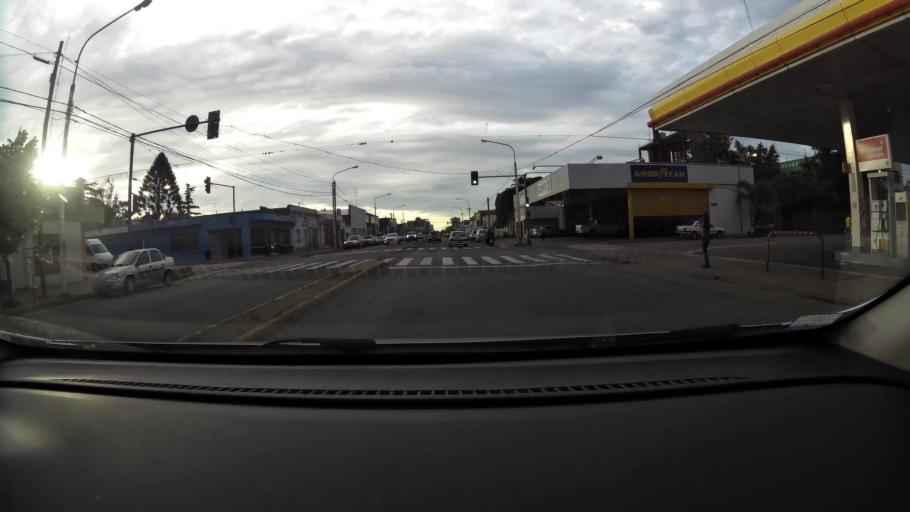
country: AR
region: Buenos Aires
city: San Nicolas de los Arroyos
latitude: -33.3445
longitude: -60.2105
